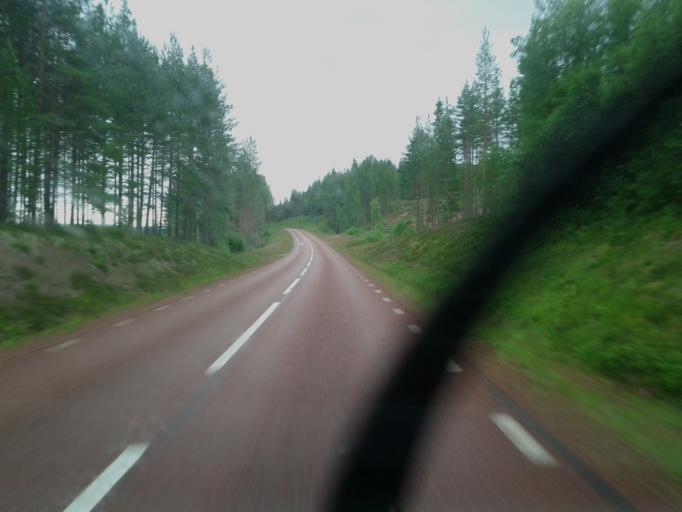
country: SE
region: Dalarna
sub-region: Alvdalens Kommun
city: AElvdalen
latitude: 61.2955
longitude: 13.7325
